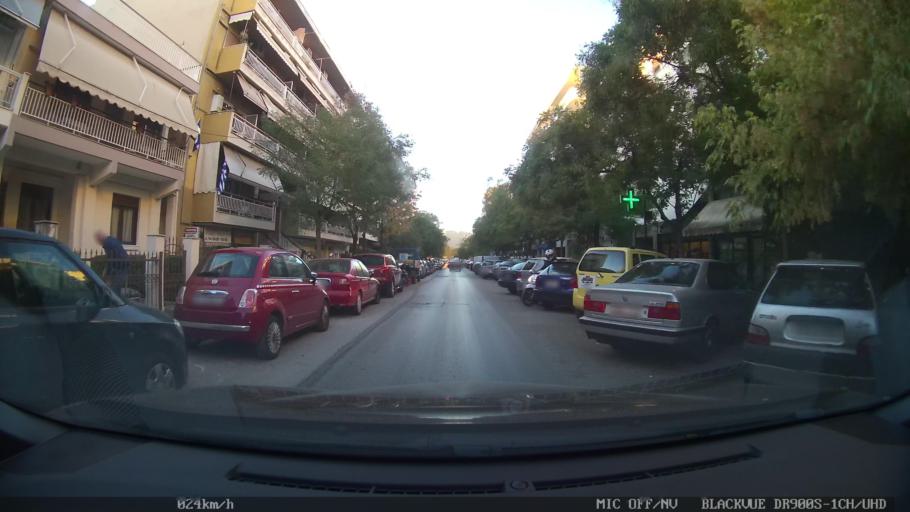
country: GR
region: Central Macedonia
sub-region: Nomos Thessalonikis
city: Triandria
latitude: 40.6082
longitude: 22.9809
